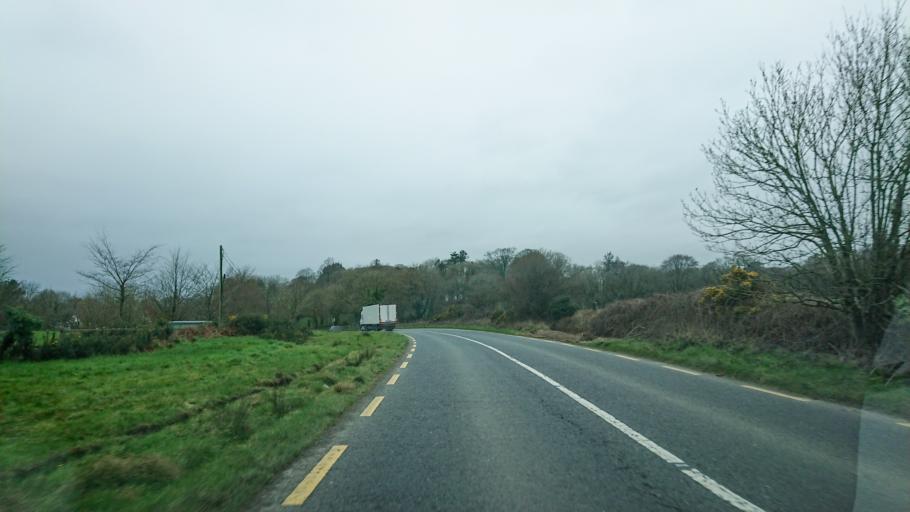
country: IE
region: Munster
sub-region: County Cork
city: Bandon
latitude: 51.7457
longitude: -8.7982
